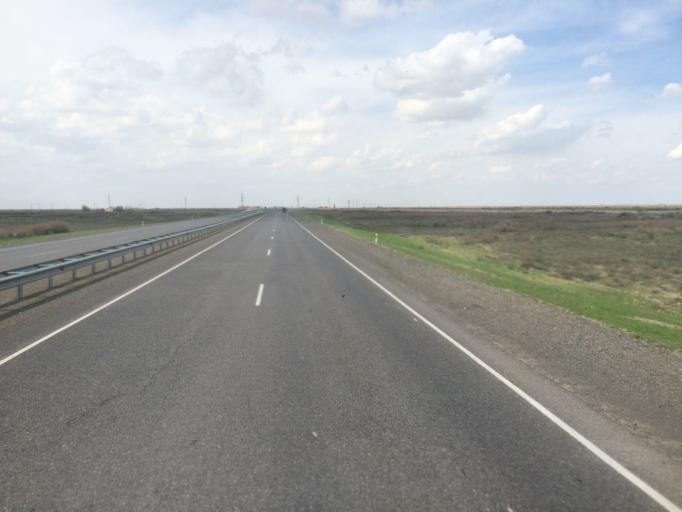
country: KZ
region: Qyzylorda
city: Zhangaqorghan
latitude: 43.9969
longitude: 67.2243
